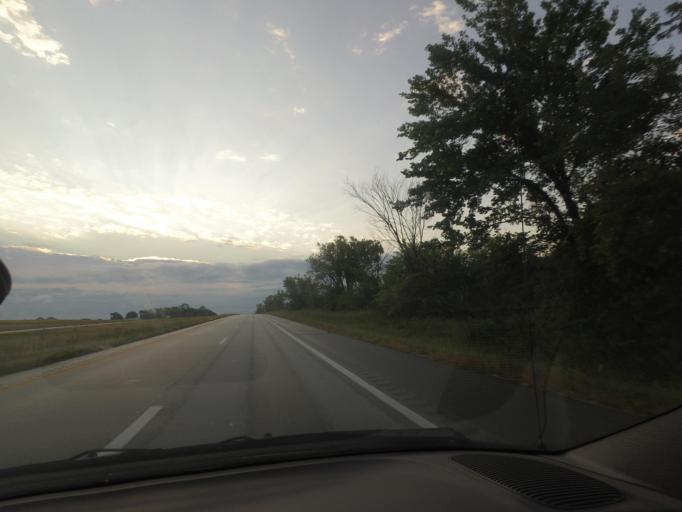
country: US
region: Missouri
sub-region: Shelby County
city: Shelbina
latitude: 39.7206
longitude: -92.1553
